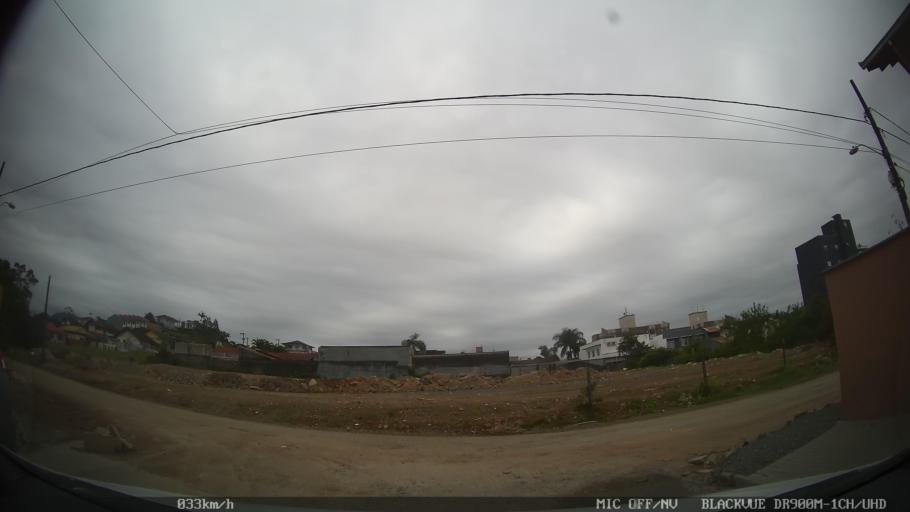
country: BR
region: Santa Catarina
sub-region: Joinville
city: Joinville
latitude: -26.2713
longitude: -48.8826
